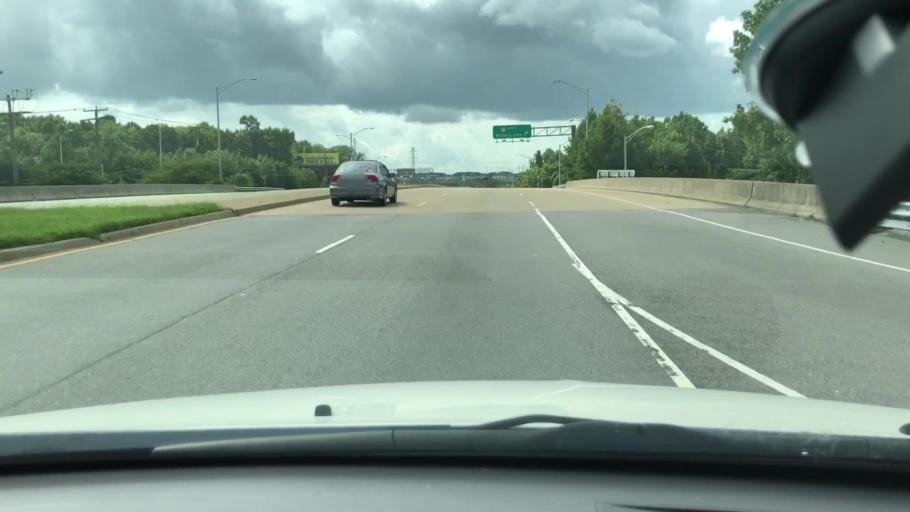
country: US
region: Virginia
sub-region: City of Chesapeake
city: Chesapeake
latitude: 36.7836
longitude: -76.2587
